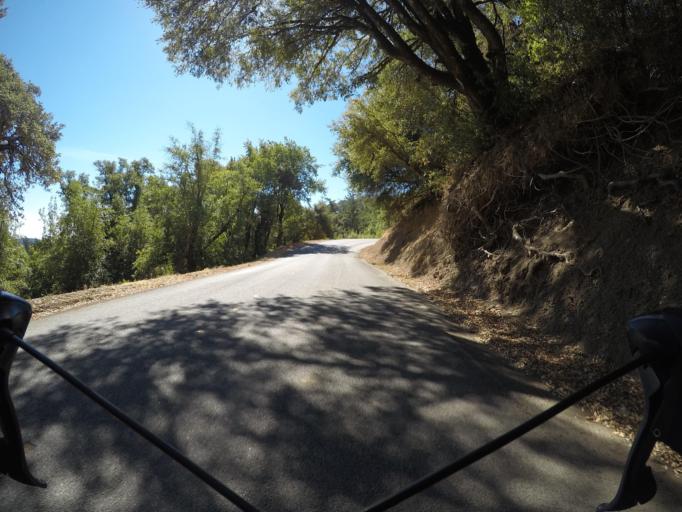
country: US
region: California
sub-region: San Mateo County
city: Portola Valley
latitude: 37.3167
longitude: -122.1958
